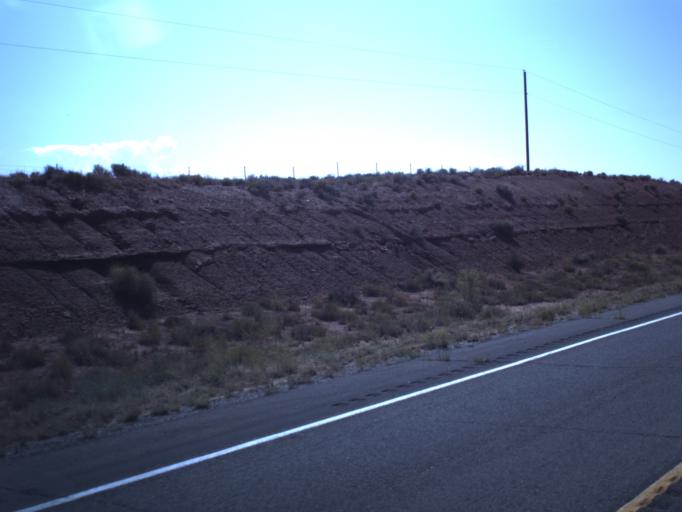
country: US
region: Utah
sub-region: San Juan County
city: Blanding
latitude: 37.0881
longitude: -109.5480
